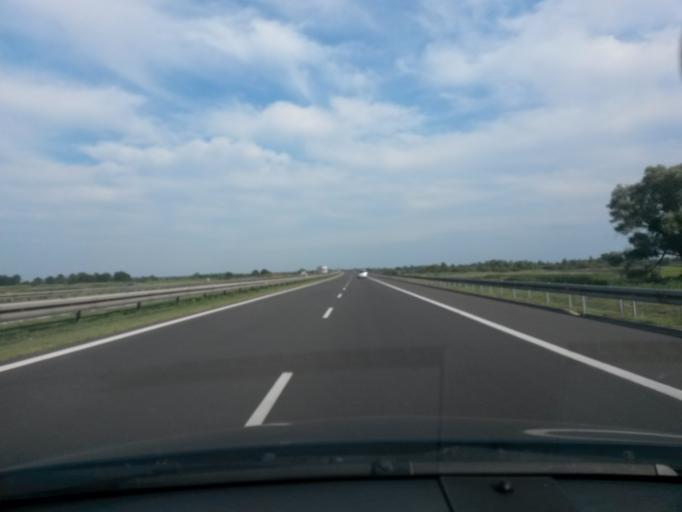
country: PL
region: Greater Poland Voivodeship
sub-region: Powiat koninski
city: Rzgow Pierwszy
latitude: 52.1998
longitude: 18.0376
